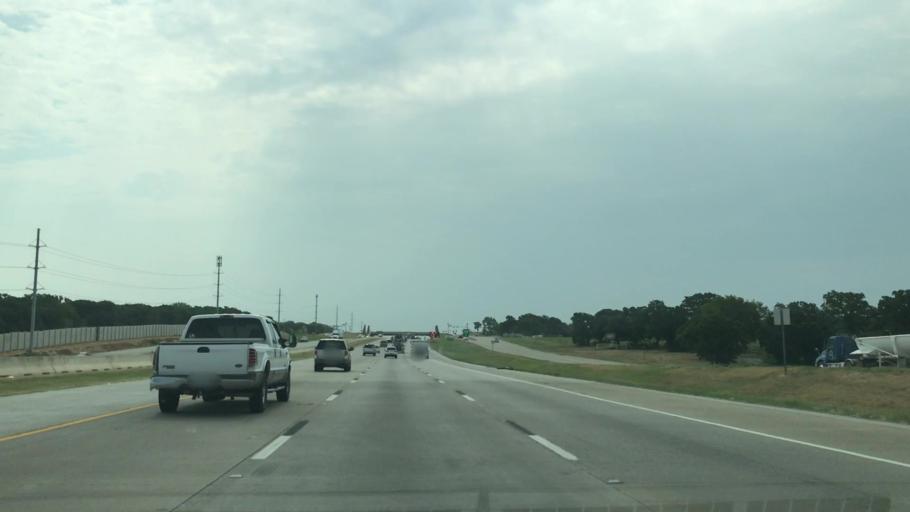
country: US
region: Texas
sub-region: Denton County
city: Trophy Club
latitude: 32.9913
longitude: -97.1886
